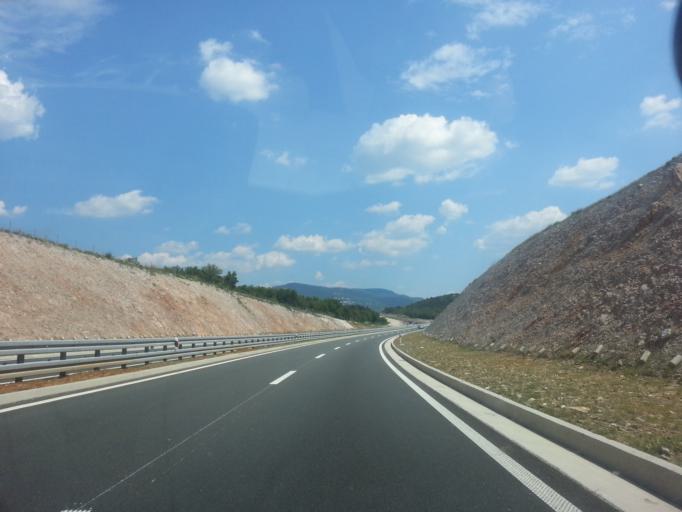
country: HR
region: Primorsko-Goranska
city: Krasica
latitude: 45.3023
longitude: 14.5594
